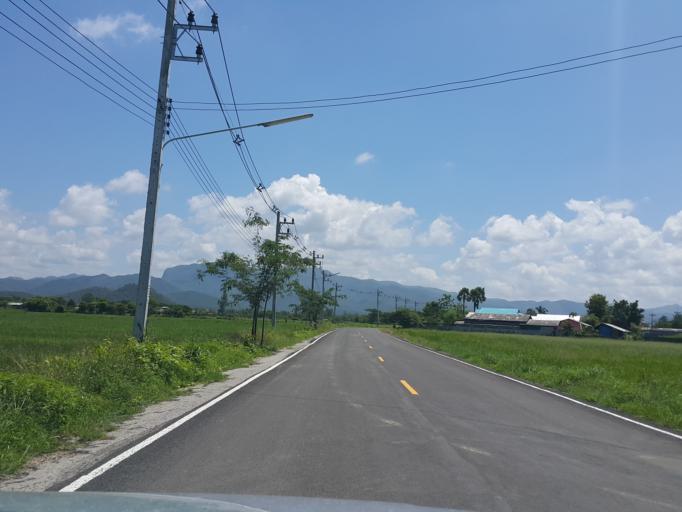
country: TH
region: Lamphun
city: Ban Thi
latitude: 18.6753
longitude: 99.1298
